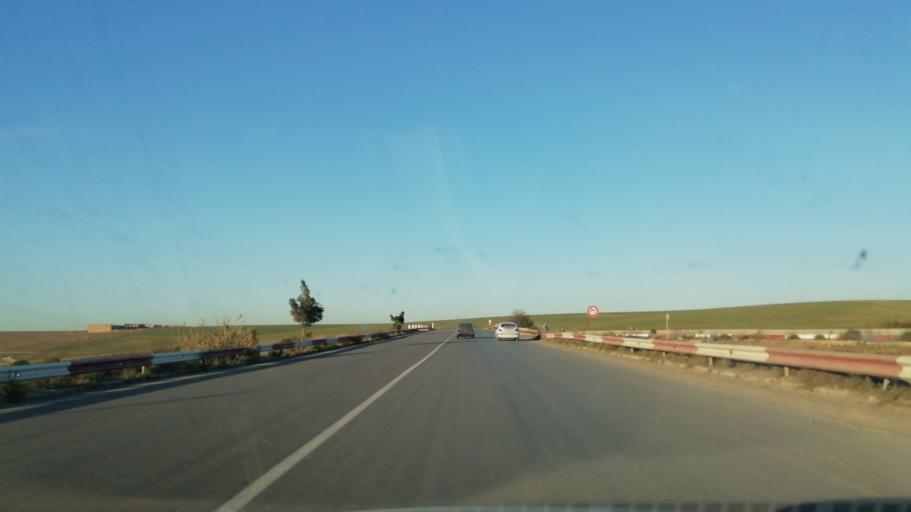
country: DZ
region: Oran
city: Sidi ech Chahmi
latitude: 35.5734
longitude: -0.5565
